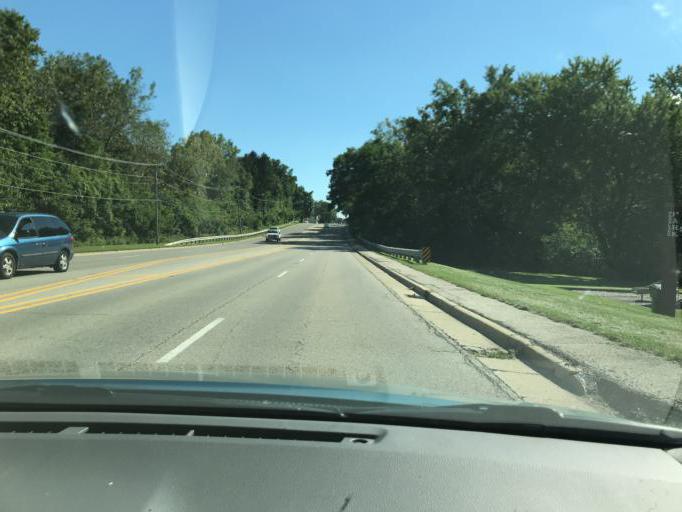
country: US
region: Illinois
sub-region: Lake County
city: Winthrop Harbor
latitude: 42.4873
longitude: -87.8221
